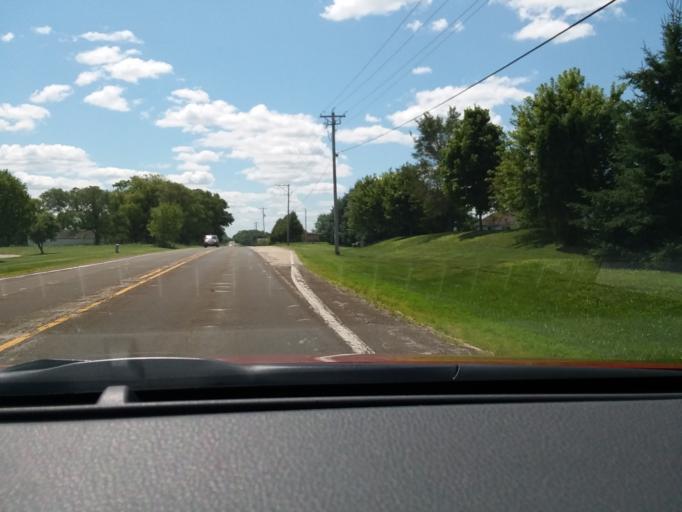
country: US
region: Wisconsin
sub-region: Dane County
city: Windsor
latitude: 43.2303
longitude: -89.3437
